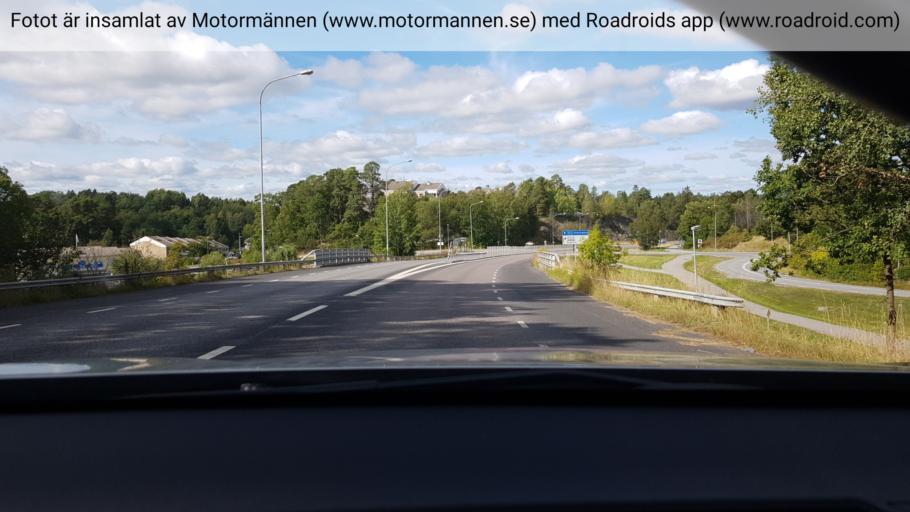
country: SE
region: Stockholm
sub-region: Vaxholms Kommun
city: Resaro
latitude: 59.4049
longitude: 18.3204
